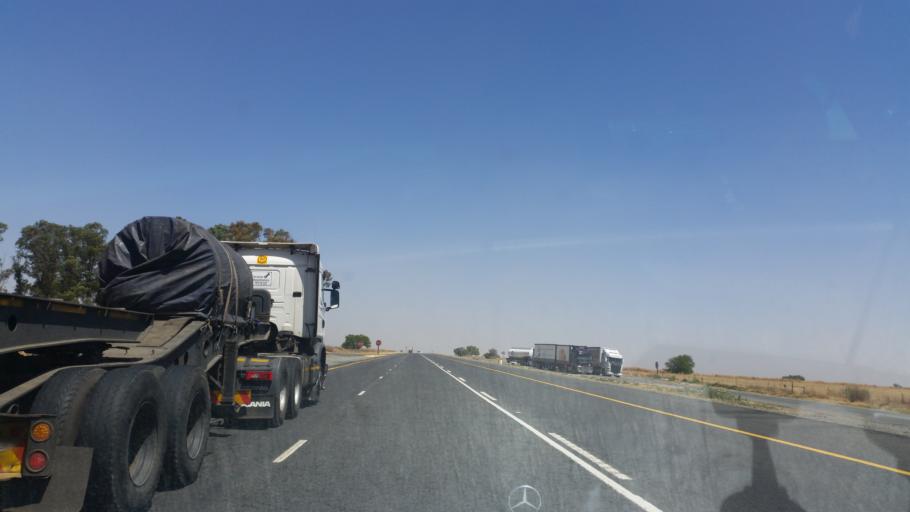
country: ZA
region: Orange Free State
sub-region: Lejweleputswa District Municipality
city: Winburg
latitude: -28.6418
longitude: 26.8885
